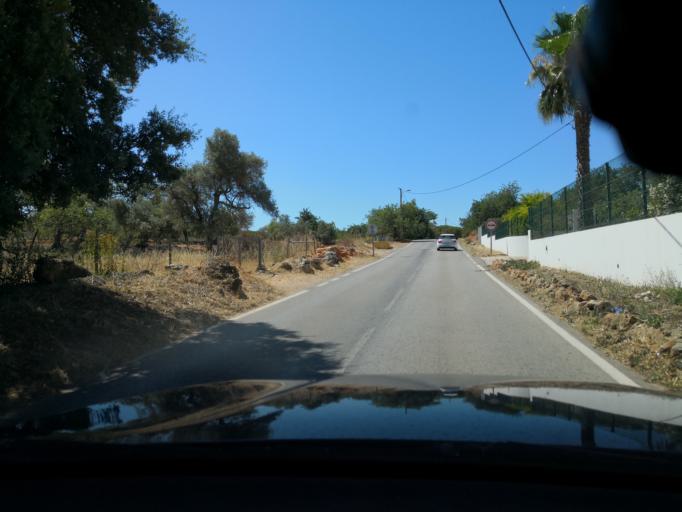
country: PT
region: Faro
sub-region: Loule
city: Vilamoura
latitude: 37.1069
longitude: -8.0964
